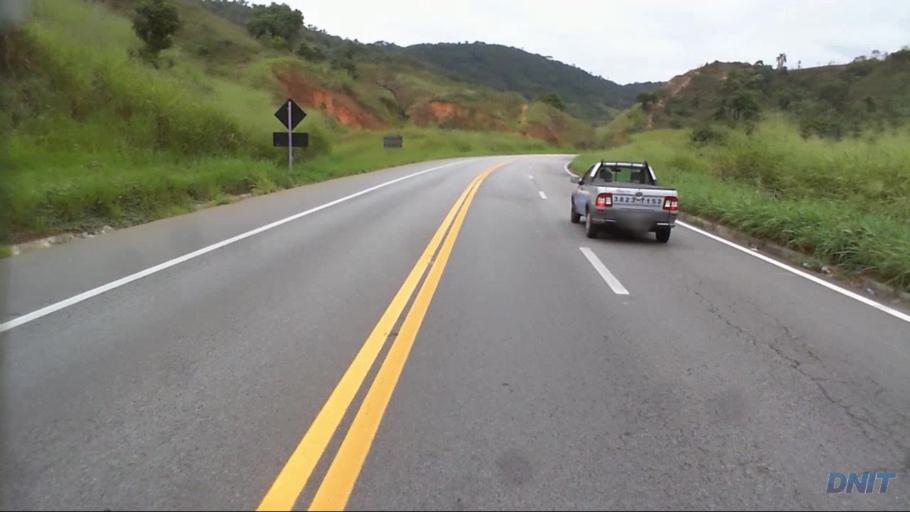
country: BR
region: Minas Gerais
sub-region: Timoteo
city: Timoteo
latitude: -19.6209
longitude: -42.8531
